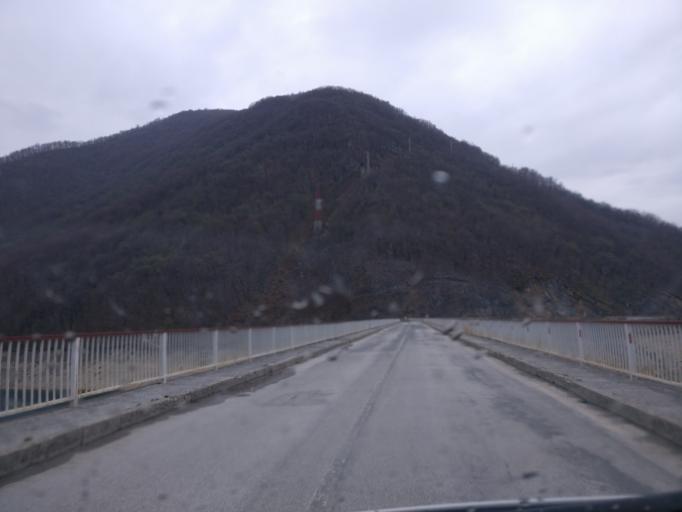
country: ME
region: Opstina Pluzine
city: Pluzine
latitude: 43.1669
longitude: 18.8570
